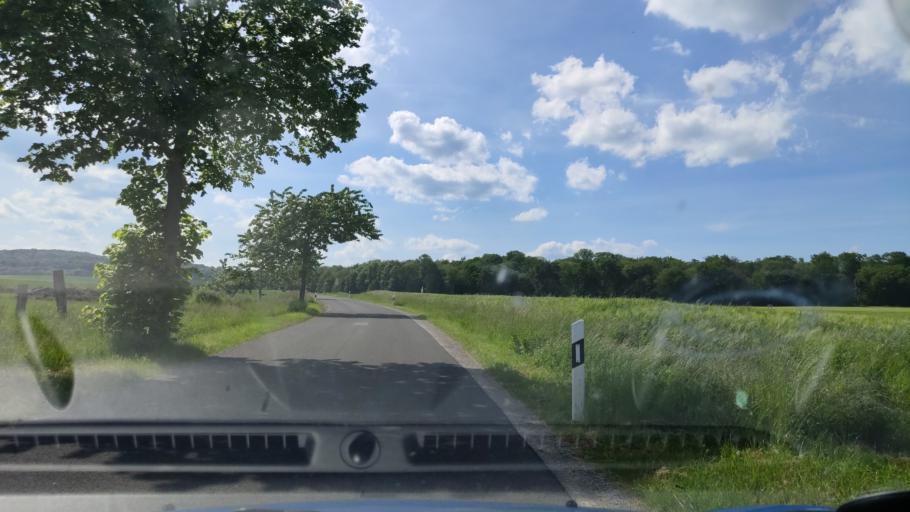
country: DE
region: Lower Saxony
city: Dransfeld
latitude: 51.5406
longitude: 9.8184
